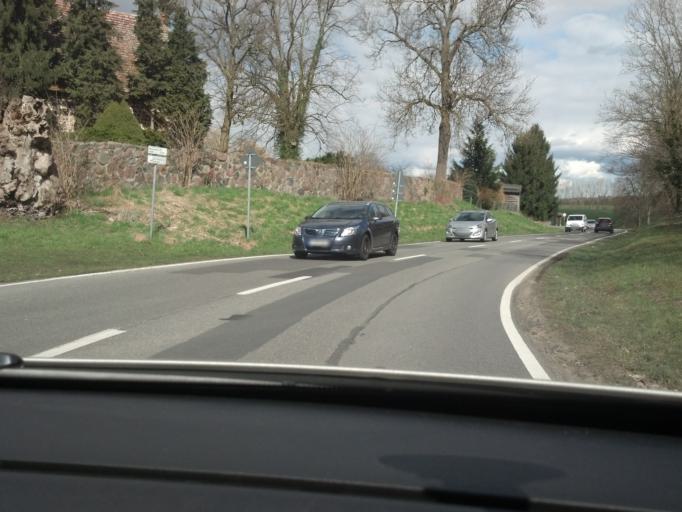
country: DE
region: Mecklenburg-Vorpommern
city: Loitz
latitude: 53.4566
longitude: 13.3590
